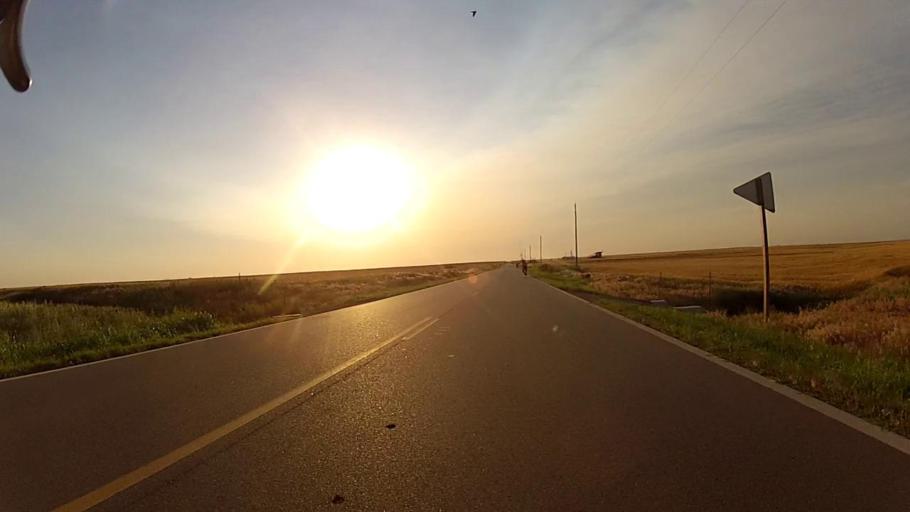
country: US
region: Kansas
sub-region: Harper County
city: Anthony
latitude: 37.1529
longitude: -97.9256
